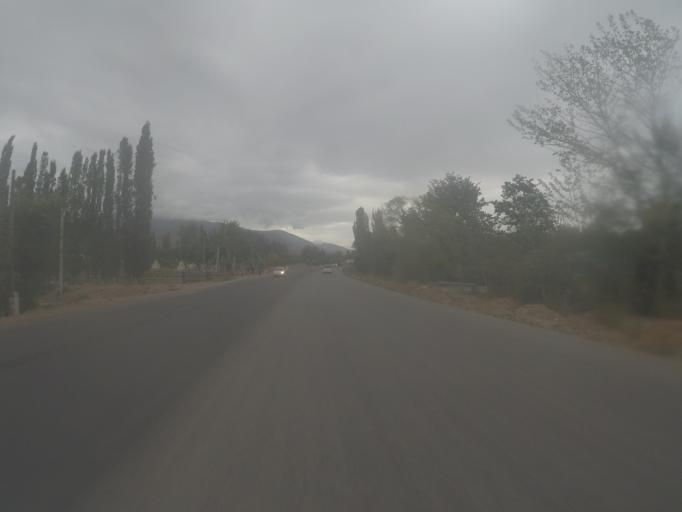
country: KG
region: Ysyk-Koel
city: Cholpon-Ata
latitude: 42.6847
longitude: 77.3388
